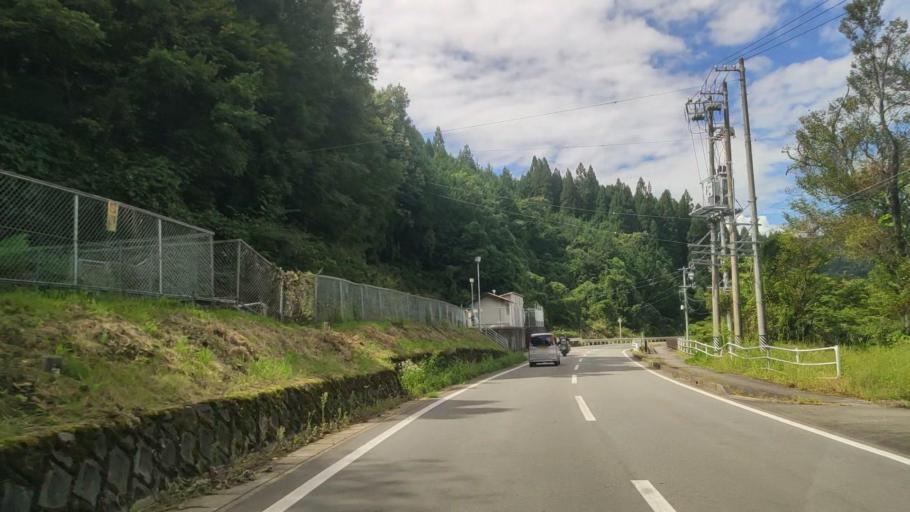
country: JP
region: Gifu
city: Takayama
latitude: 36.1815
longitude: 137.2590
